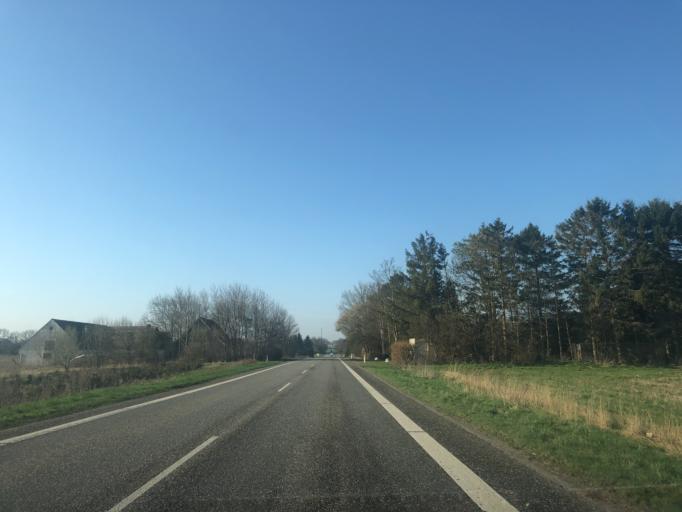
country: DK
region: Zealand
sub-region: Faxe Kommune
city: Ronnede
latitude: 55.2704
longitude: 12.0275
